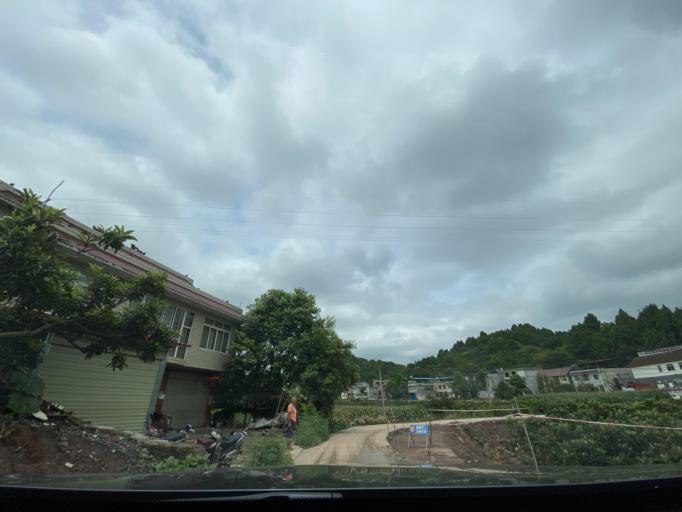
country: CN
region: Sichuan
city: Jiancheng
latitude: 30.4029
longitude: 104.5733
